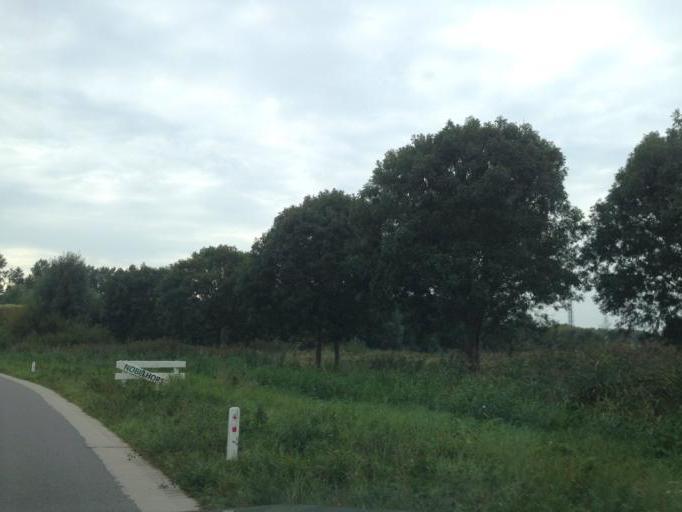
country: NL
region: Flevoland
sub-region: Gemeente Almere
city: Almere Stad
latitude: 52.3741
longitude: 5.2949
